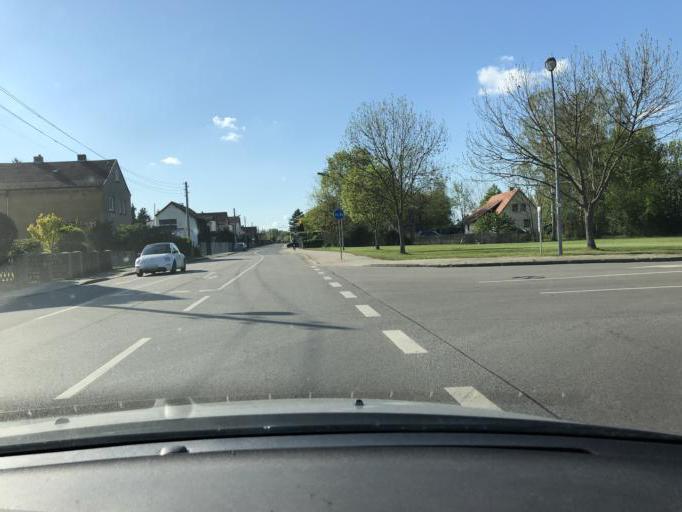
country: DE
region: Saxony
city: Regis-Breitingen
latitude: 51.0939
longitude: 12.4427
